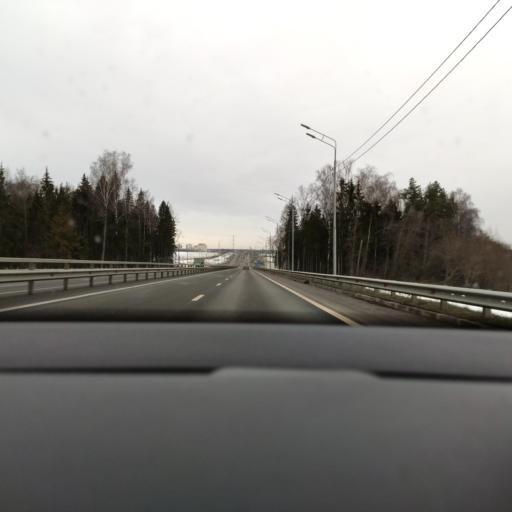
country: RU
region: Moskovskaya
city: Zvenigorod
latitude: 55.6844
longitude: 36.8911
